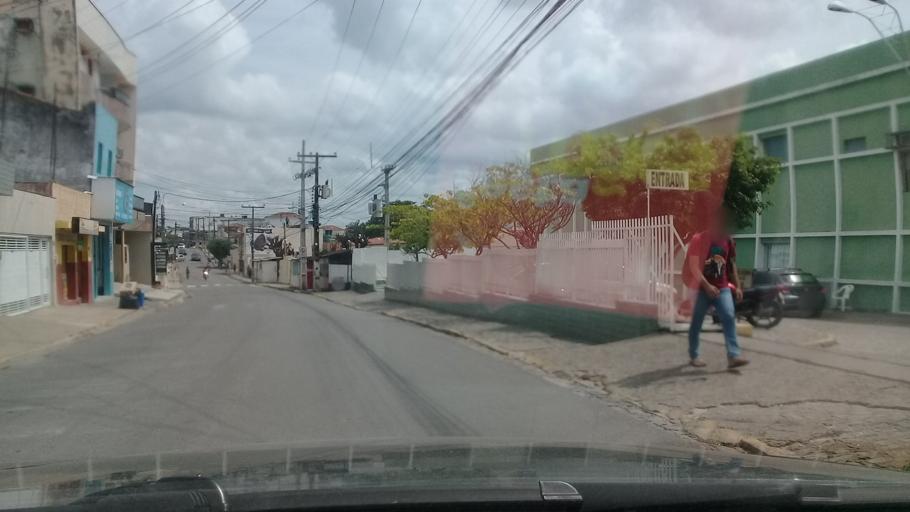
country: BR
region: Pernambuco
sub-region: Vitoria De Santo Antao
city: Vitoria de Santo Antao
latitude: -8.1136
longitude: -35.2888
